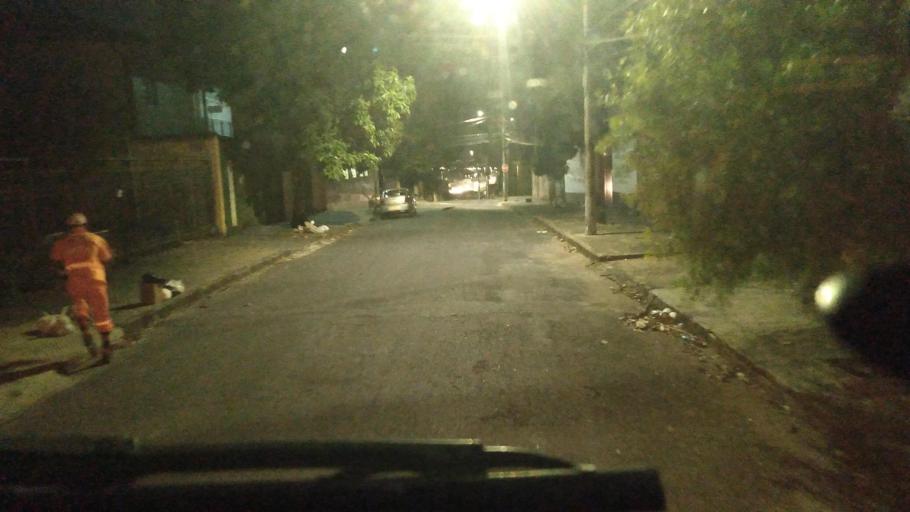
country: BR
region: Minas Gerais
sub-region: Belo Horizonte
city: Belo Horizonte
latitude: -19.8835
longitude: -43.9547
